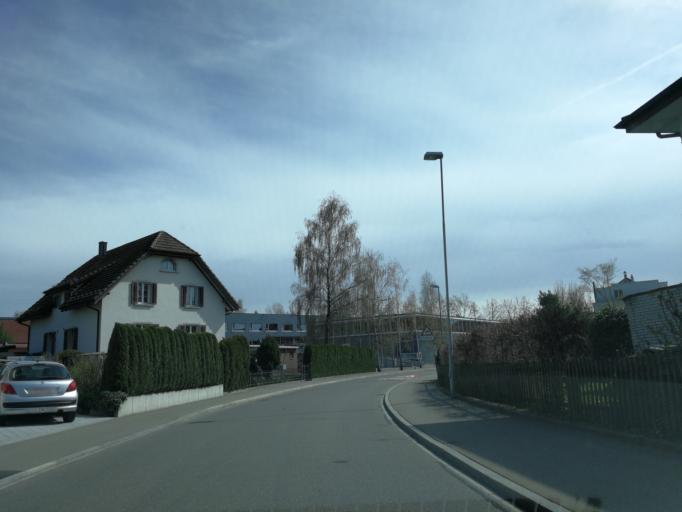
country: CH
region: Zurich
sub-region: Bezirk Meilen
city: Uetikon / Grossdorf
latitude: 47.2651
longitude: 8.6775
